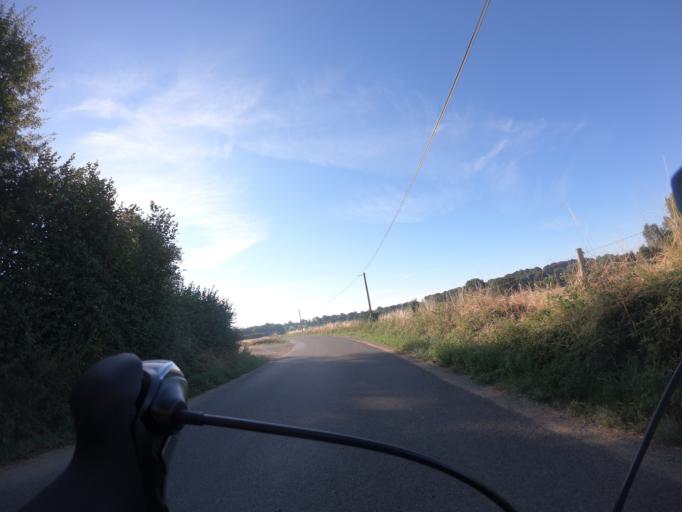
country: FR
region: Pays de la Loire
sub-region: Departement de la Mayenne
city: Pre-en-Pail
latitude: 48.5444
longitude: -0.2279
